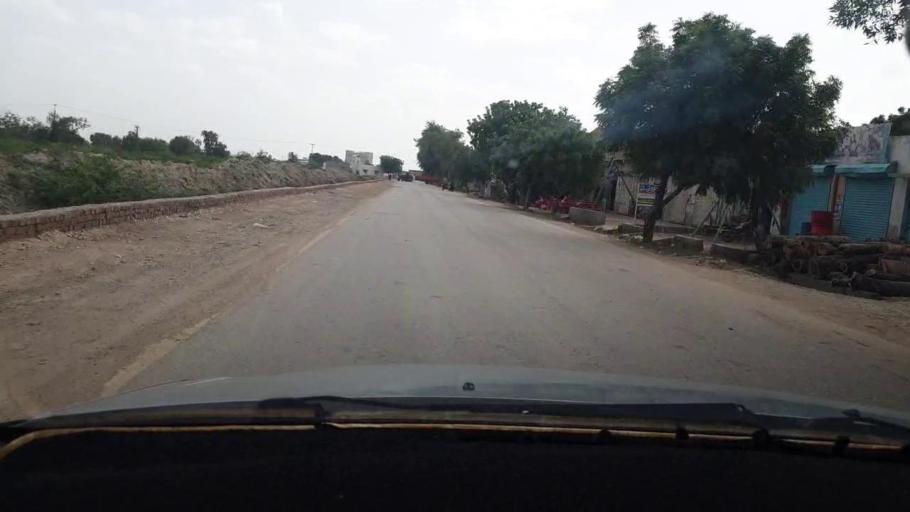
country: PK
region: Sindh
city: Digri
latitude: 25.0650
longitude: 69.2178
